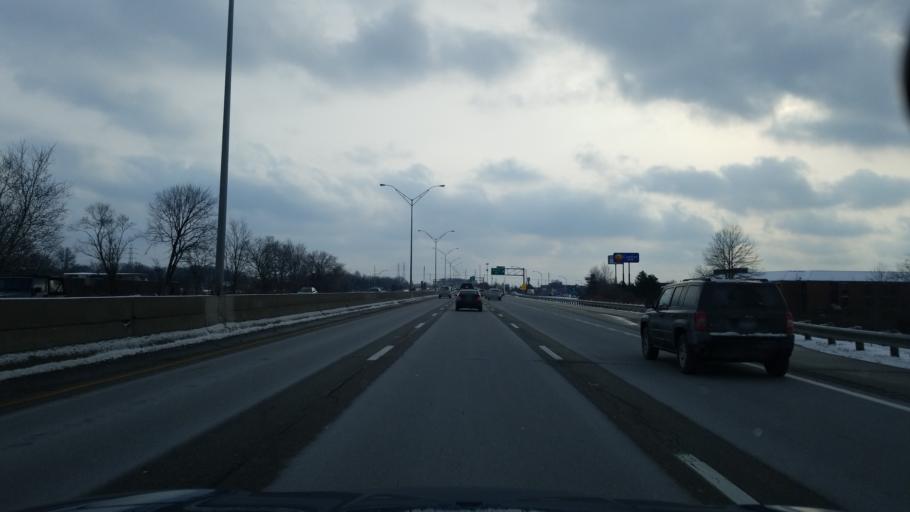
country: US
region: Ohio
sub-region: Cuyahoga County
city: Middleburg Heights
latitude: 41.3771
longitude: -81.8197
